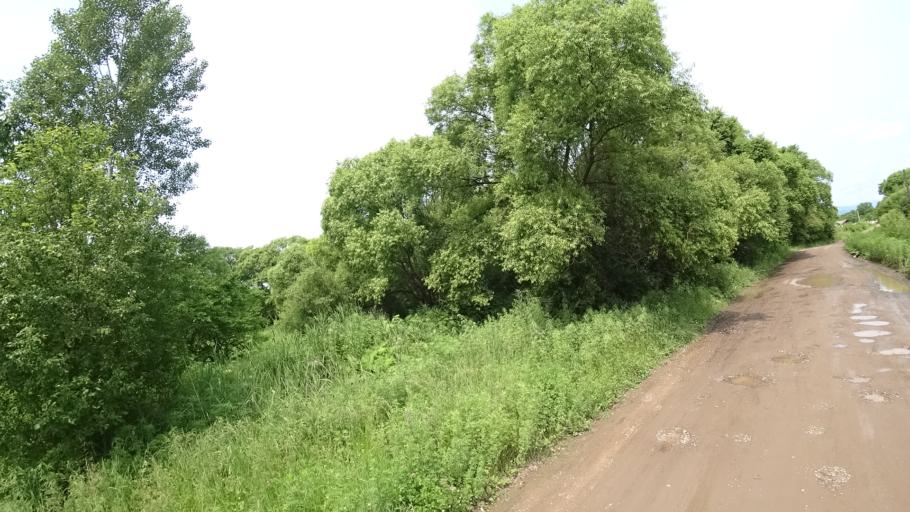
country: RU
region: Primorskiy
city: Novosysoyevka
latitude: 44.2517
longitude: 133.3755
